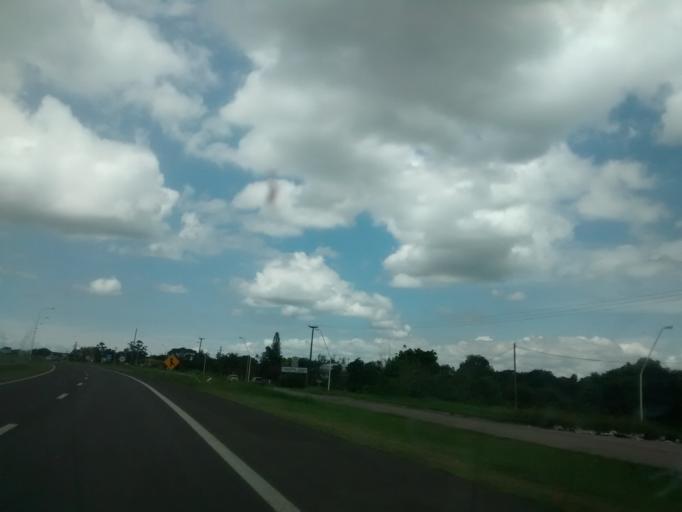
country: AR
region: Chaco
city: Fontana
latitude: -27.4123
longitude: -58.9950
